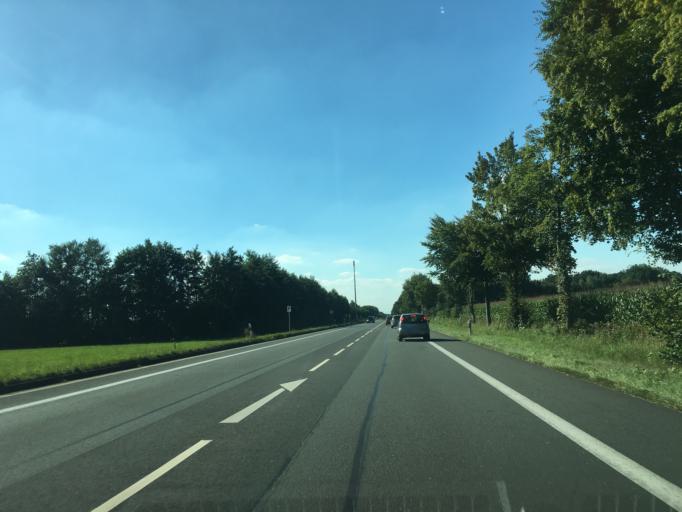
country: DE
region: North Rhine-Westphalia
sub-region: Regierungsbezirk Munster
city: Beelen
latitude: 51.9131
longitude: 8.1655
